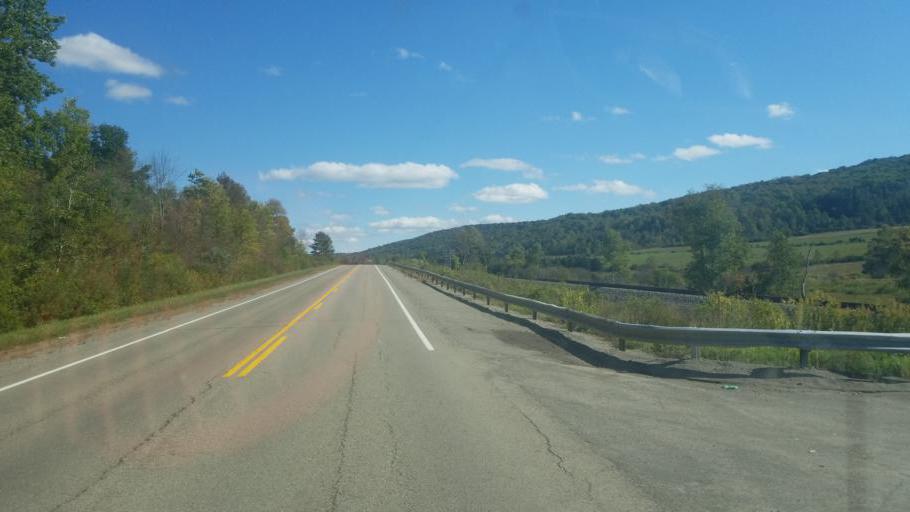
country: US
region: New York
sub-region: Allegany County
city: Cuba
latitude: 42.2182
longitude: -78.2364
